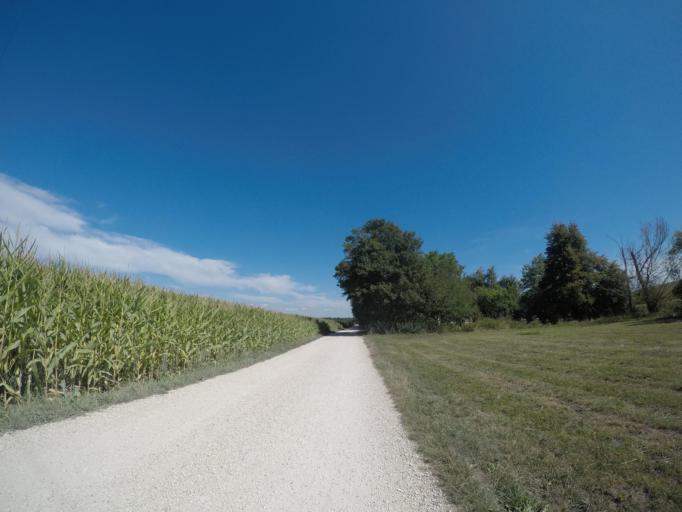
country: DE
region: Bavaria
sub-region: Swabia
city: Senden
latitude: 48.3624
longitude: 10.0568
